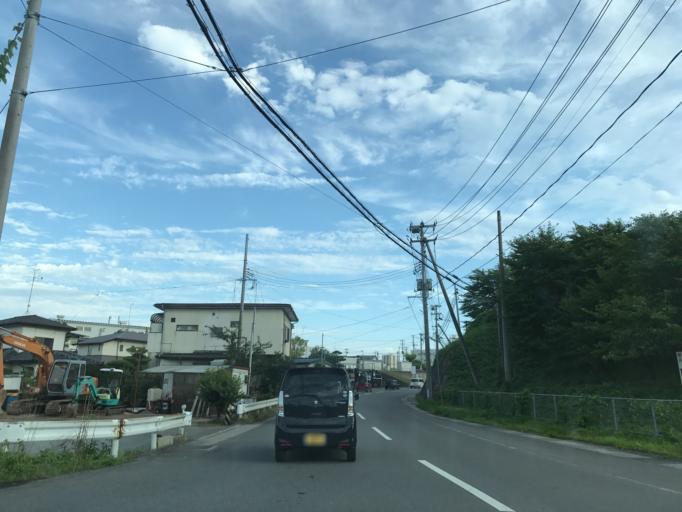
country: JP
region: Fukushima
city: Sukagawa
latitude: 37.3122
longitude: 140.3606
